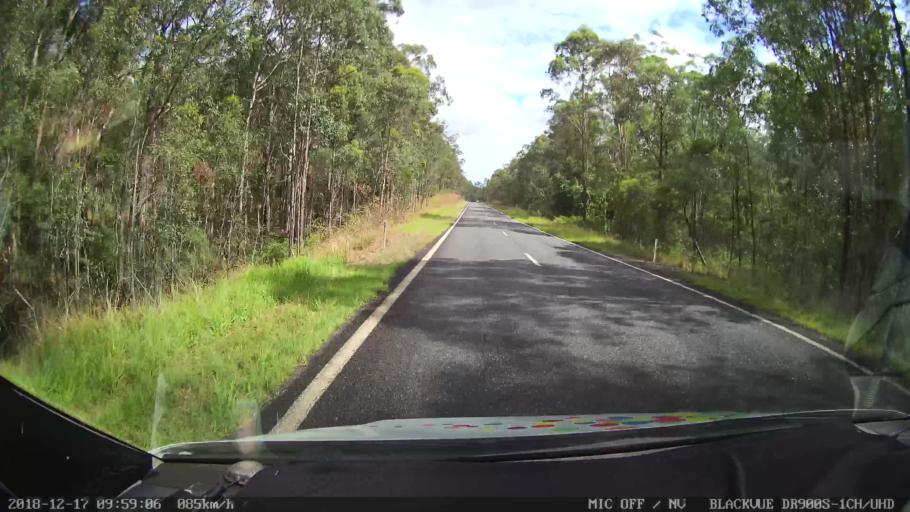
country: AU
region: New South Wales
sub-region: Tenterfield Municipality
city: Carrolls Creek
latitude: -28.9143
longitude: 152.4146
